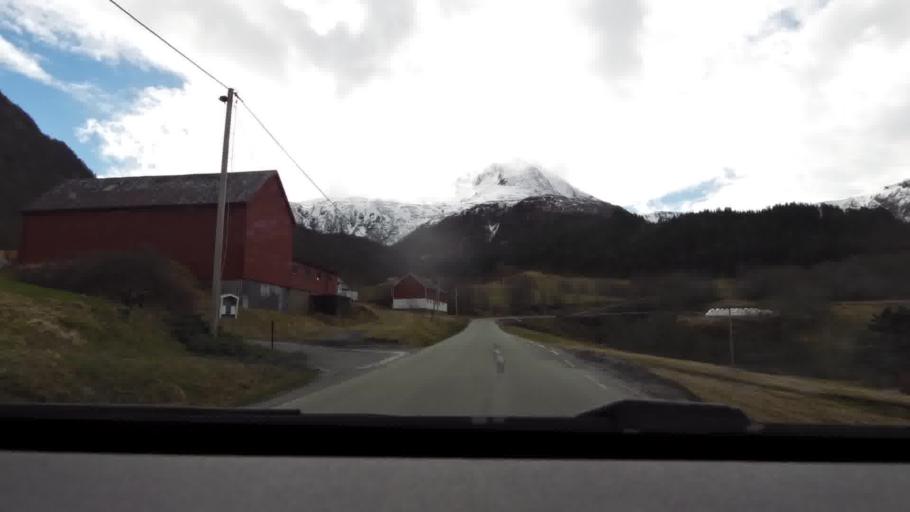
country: NO
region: More og Romsdal
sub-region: Gjemnes
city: Batnfjordsora
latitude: 62.9315
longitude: 7.6052
